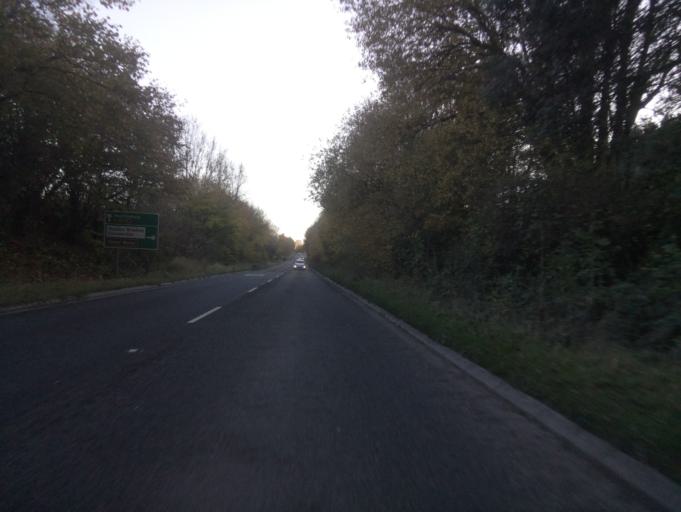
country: GB
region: England
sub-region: Wiltshire
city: Warminster
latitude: 51.1785
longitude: -2.1948
